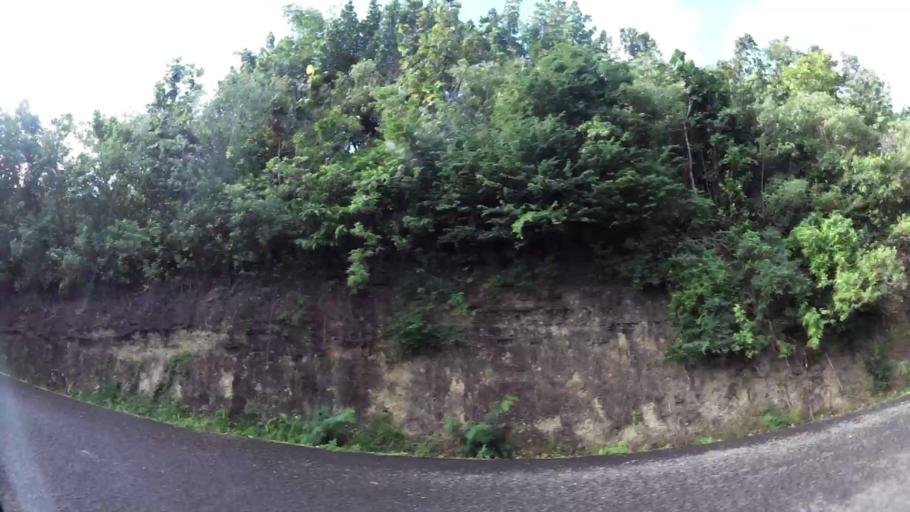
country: LC
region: Anse-la-Raye
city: Canaries
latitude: 13.8976
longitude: -61.0623
